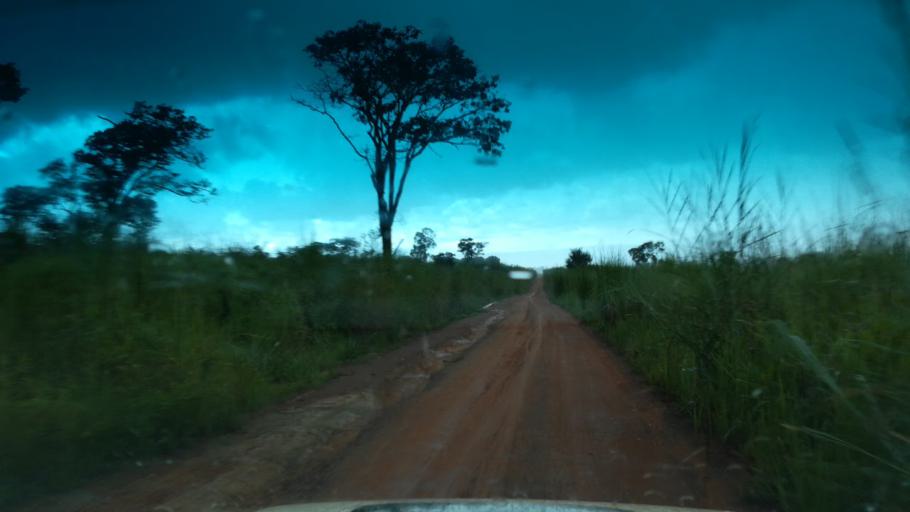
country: ZM
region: Northern
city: Kaputa
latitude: -7.6727
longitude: 29.2424
